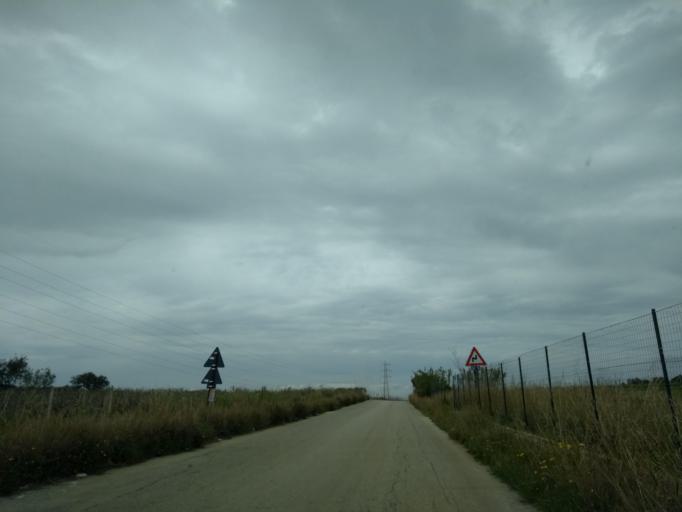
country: IT
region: Sicily
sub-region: Palermo
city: Partinico
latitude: 37.9919
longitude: 13.0672
